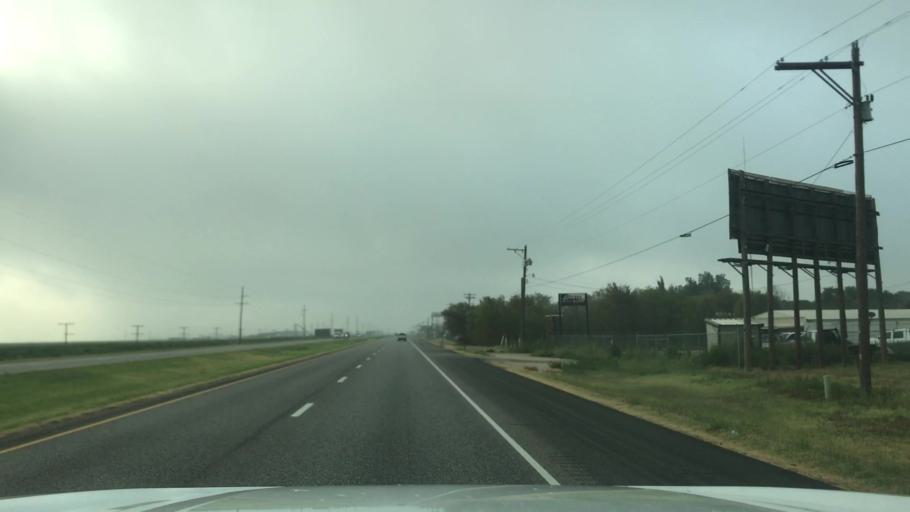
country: US
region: Texas
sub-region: Lubbock County
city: Ransom Canyon
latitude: 33.4970
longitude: -101.7367
